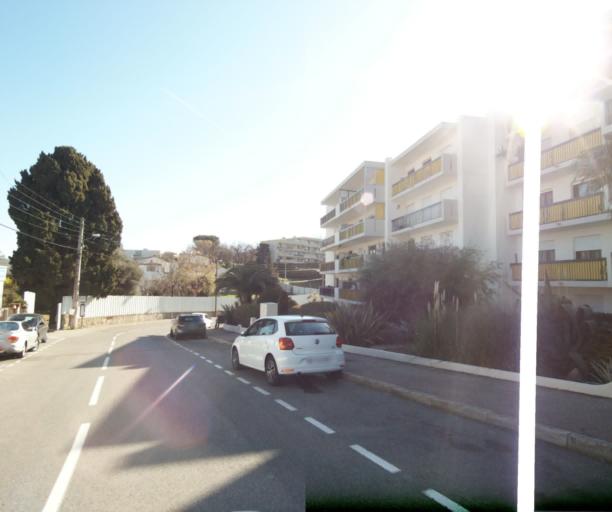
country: FR
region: Provence-Alpes-Cote d'Azur
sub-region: Departement des Alpes-Maritimes
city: Antibes
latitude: 43.5920
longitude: 7.1099
